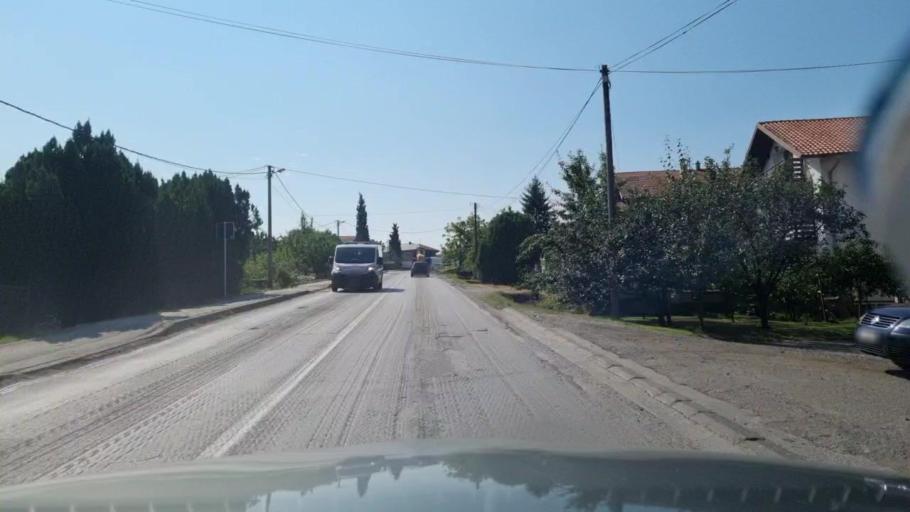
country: BA
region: Federation of Bosnia and Herzegovina
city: Gradacac
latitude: 44.8710
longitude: 18.4299
